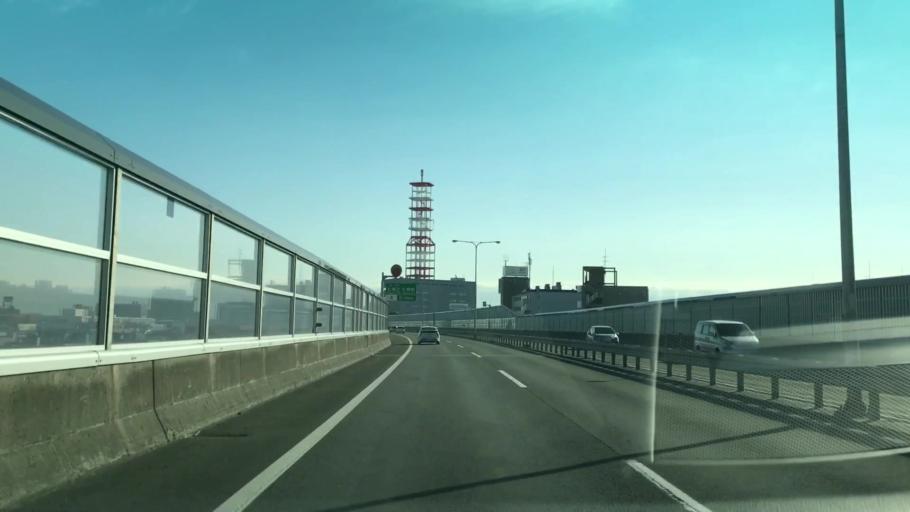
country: JP
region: Hokkaido
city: Sapporo
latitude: 43.1009
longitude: 141.3286
